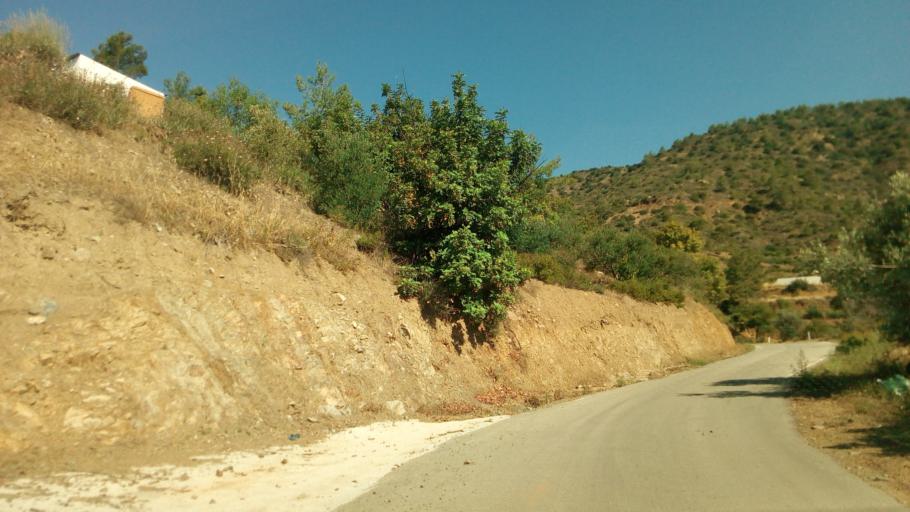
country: CY
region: Limassol
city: Parekklisha
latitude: 34.8699
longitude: 33.1785
